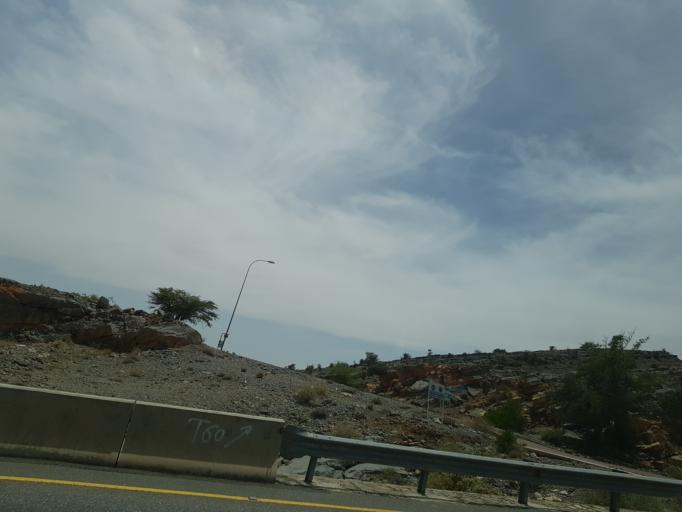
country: OM
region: Muhafazat ad Dakhiliyah
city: Izki
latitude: 23.0099
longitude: 57.6989
